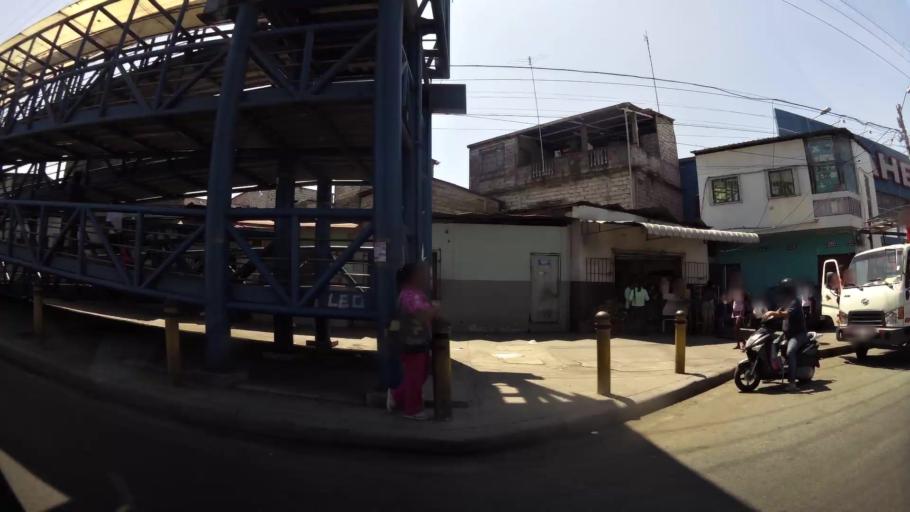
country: EC
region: Guayas
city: Guayaquil
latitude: -2.2397
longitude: -79.9202
